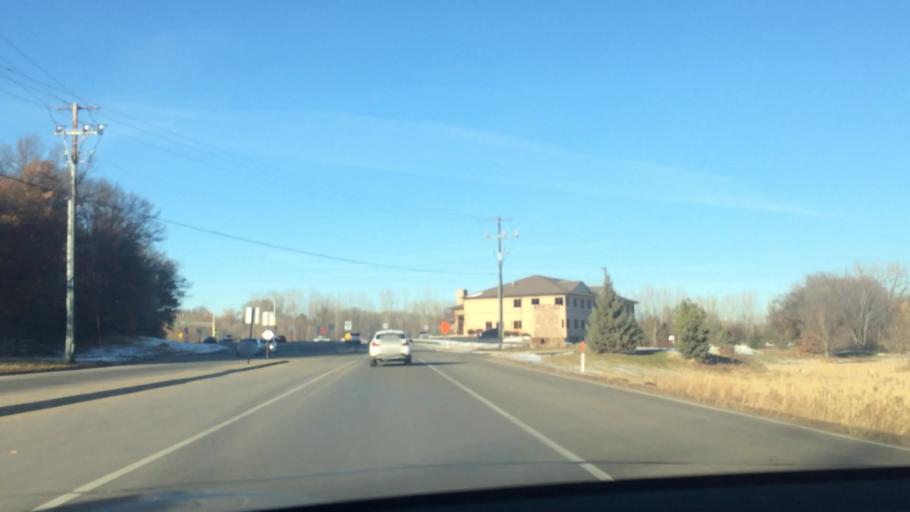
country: US
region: Minnesota
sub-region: Anoka County
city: Circle Pines
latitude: 45.1512
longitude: -93.1354
